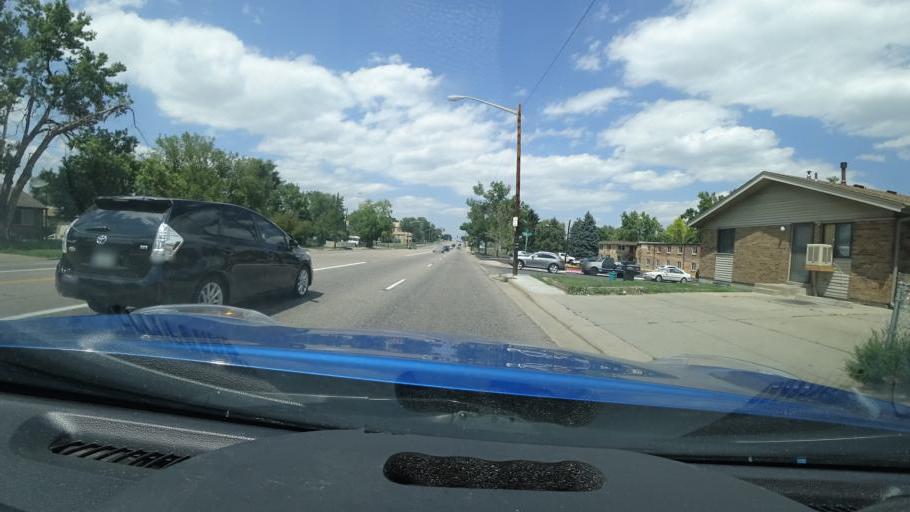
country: US
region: Colorado
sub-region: Arapahoe County
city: Sheridan
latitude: 39.6698
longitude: -105.0250
